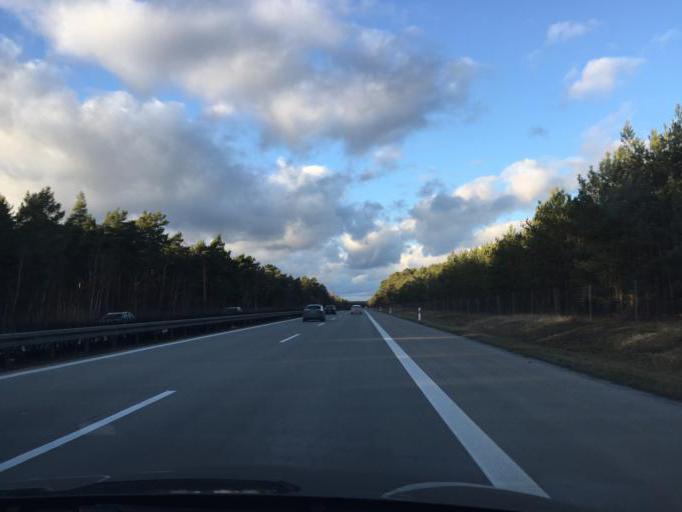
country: DE
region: Brandenburg
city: Halbe
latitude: 52.0364
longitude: 13.6720
